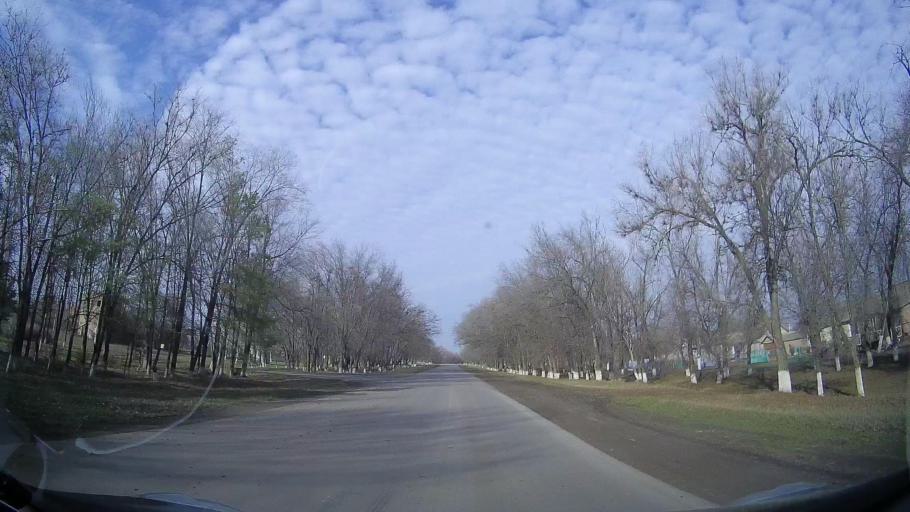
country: RU
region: Rostov
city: Gigant
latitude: 46.8365
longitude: 41.3332
